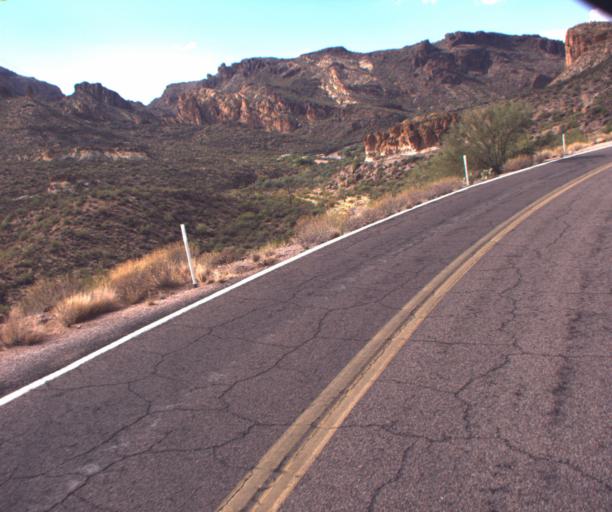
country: US
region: Arizona
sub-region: Pinal County
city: Apache Junction
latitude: 33.5309
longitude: -111.3816
